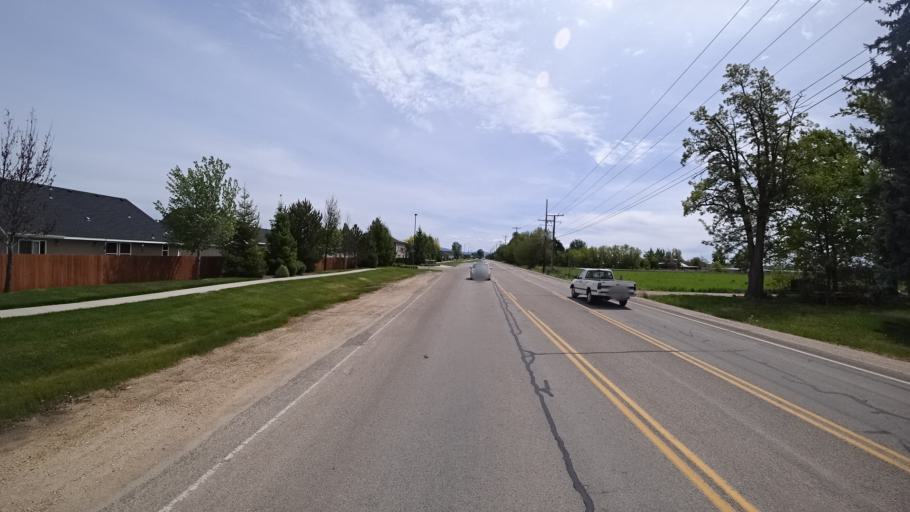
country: US
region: Idaho
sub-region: Ada County
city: Meridian
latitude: 43.5613
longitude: -116.3713
